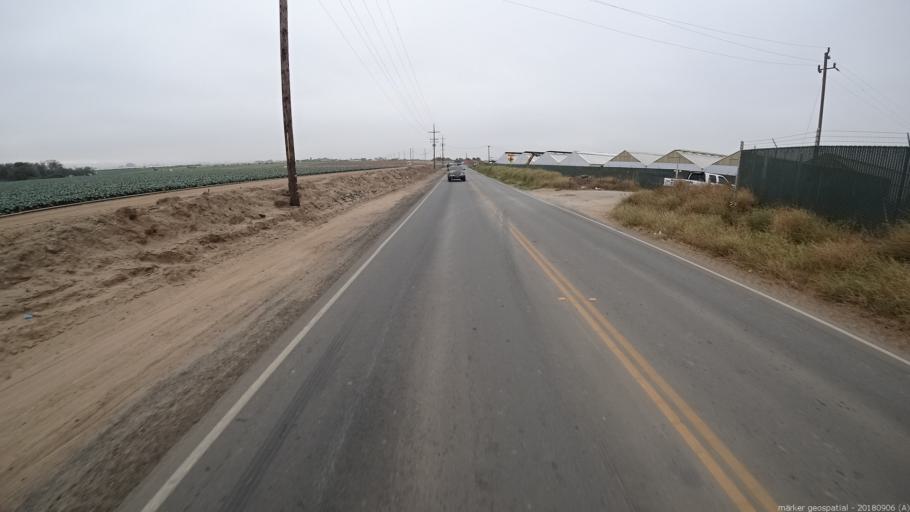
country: US
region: California
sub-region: Monterey County
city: Salinas
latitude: 36.6470
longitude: -121.5782
